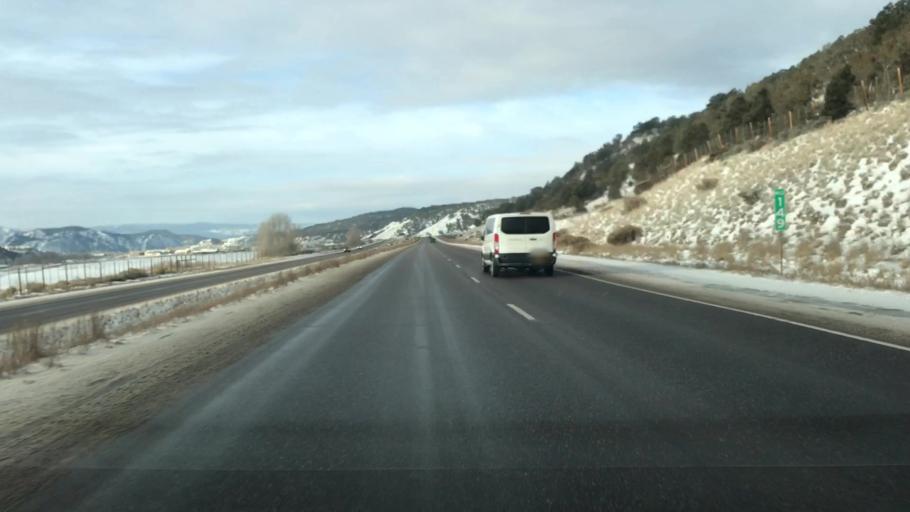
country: US
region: Colorado
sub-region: Eagle County
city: Eagle
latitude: 39.6750
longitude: -106.7880
